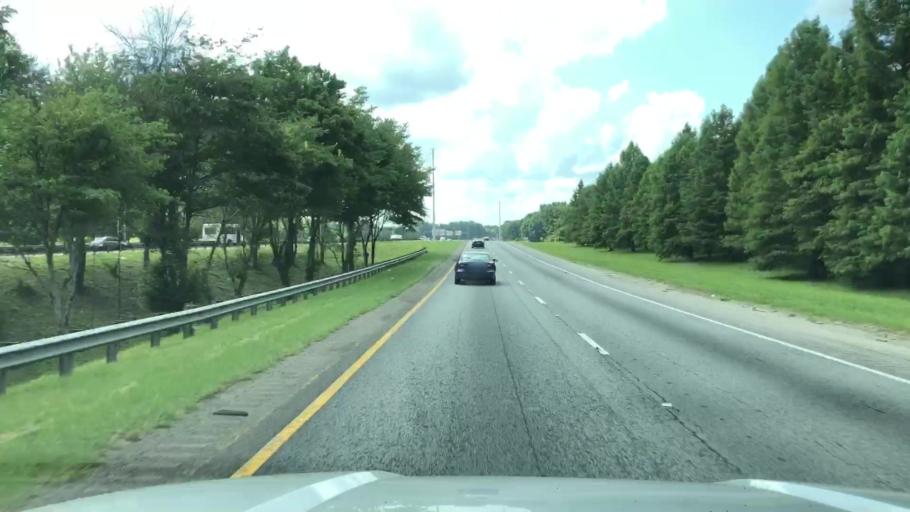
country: US
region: Georgia
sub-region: Fulton County
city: College Park
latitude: 33.6150
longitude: -84.4872
